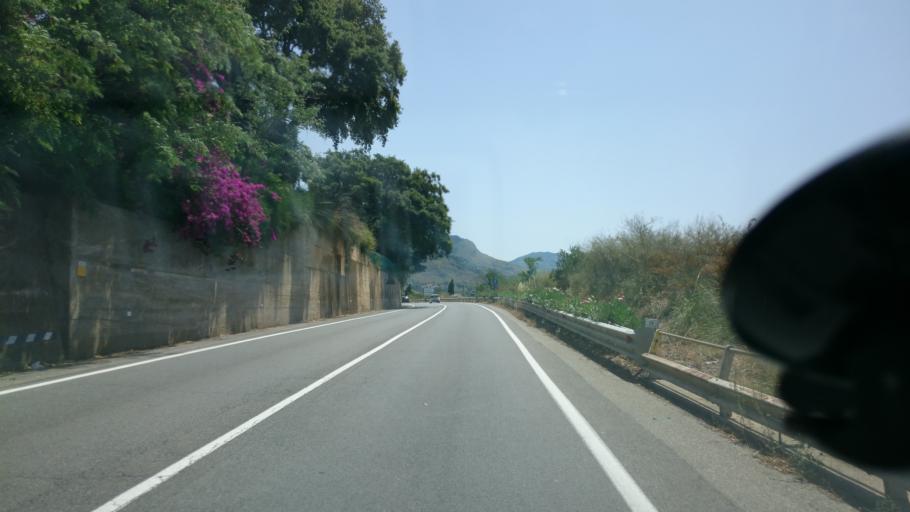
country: IT
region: Calabria
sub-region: Provincia di Cosenza
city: Cittadella del Capo
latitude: 39.5392
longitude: 15.8995
